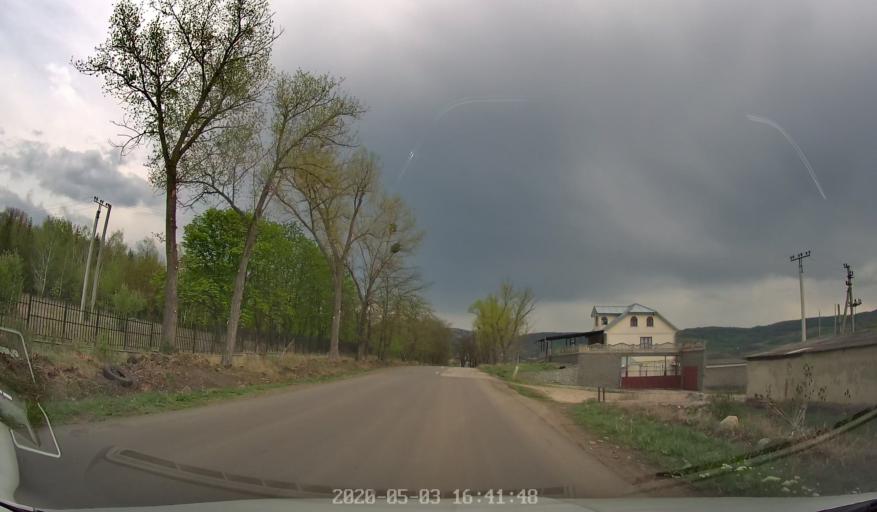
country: MD
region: Stinga Nistrului
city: Bucovat
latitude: 47.1636
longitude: 28.4128
